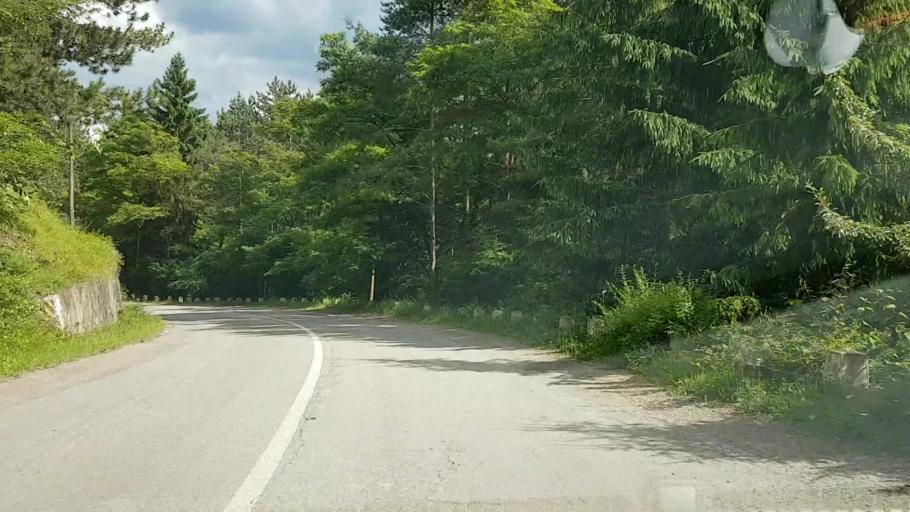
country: RO
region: Neamt
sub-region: Comuna Hangu
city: Hangu
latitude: 47.0529
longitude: 26.0010
